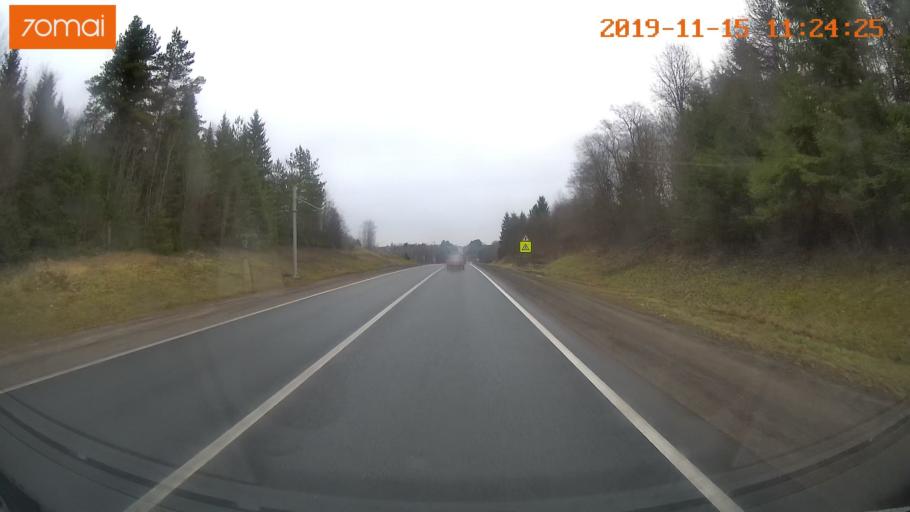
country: RU
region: Vologda
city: Molochnoye
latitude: 59.1569
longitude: 39.4042
